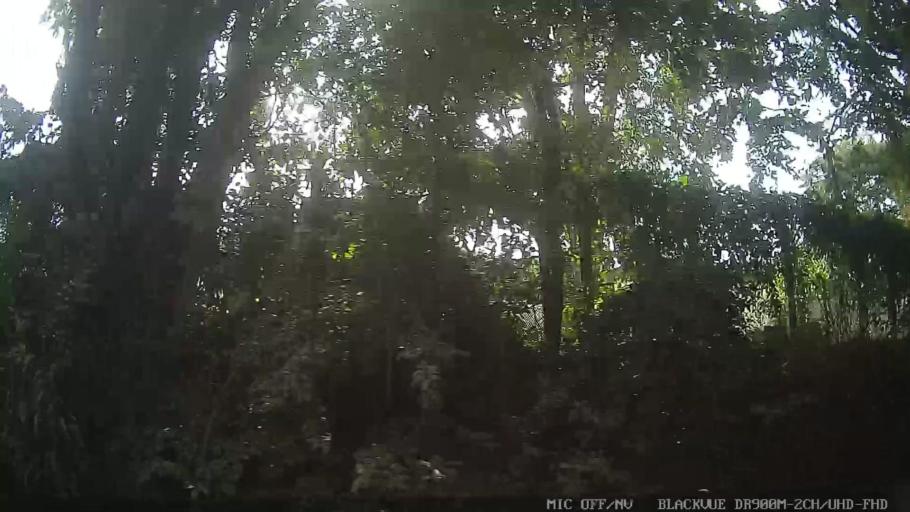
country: BR
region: Sao Paulo
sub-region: Jarinu
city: Jarinu
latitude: -23.0416
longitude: -46.6419
